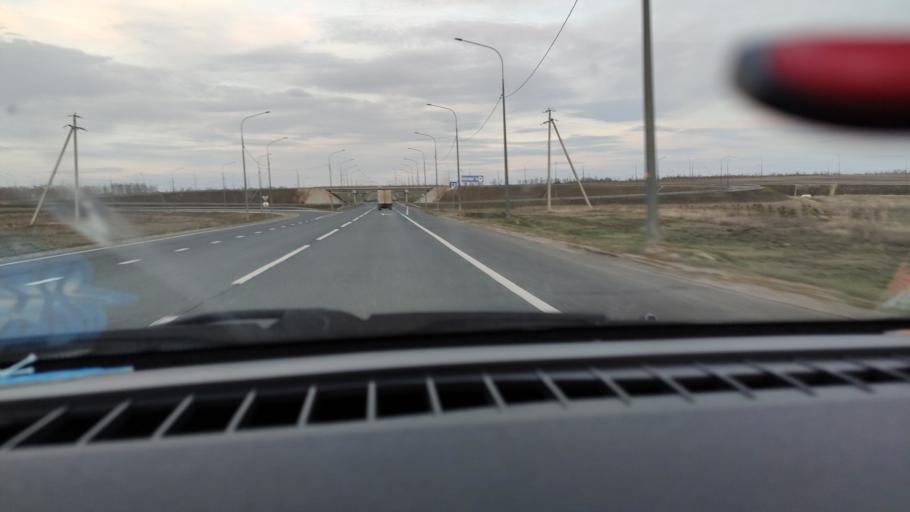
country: RU
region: Saratov
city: Yelshanka
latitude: 51.8305
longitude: 46.4240
